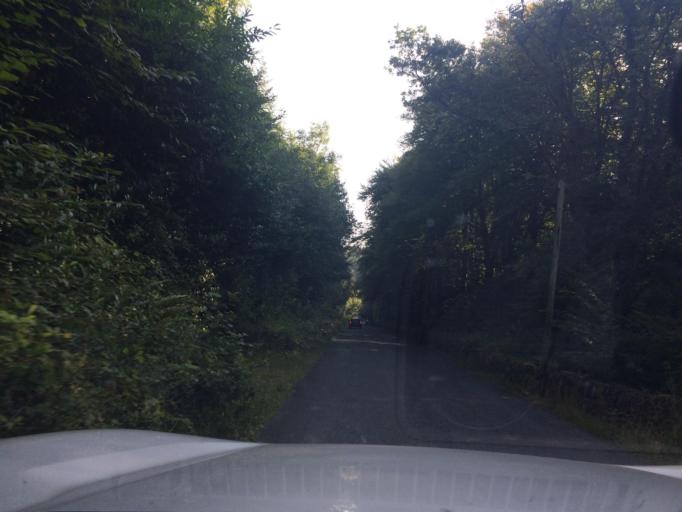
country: IE
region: Munster
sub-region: Waterford
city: Dungarvan
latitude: 52.1296
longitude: -7.6835
